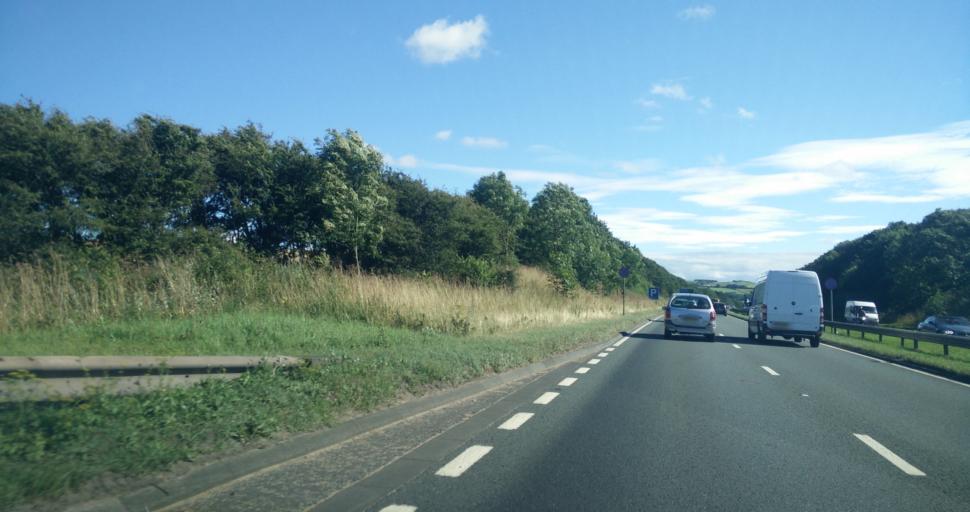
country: GB
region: England
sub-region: County Durham
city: Houghton-le-Spring
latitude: 54.8794
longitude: -1.4530
